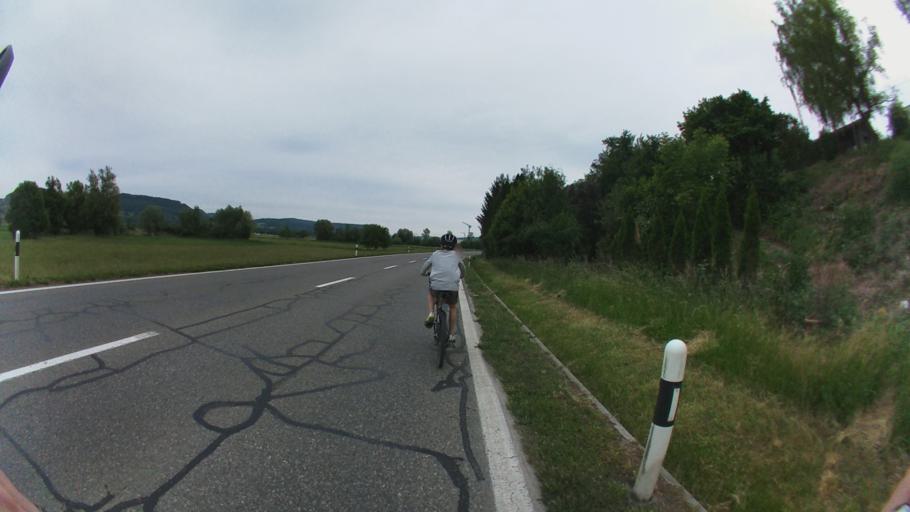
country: CH
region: Aargau
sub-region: Bezirk Zurzach
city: Bad Zurzach
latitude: 47.5991
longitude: 8.2819
